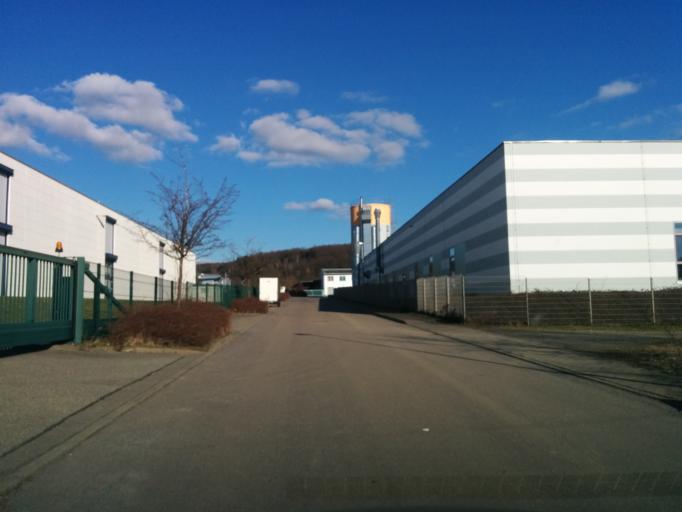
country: DE
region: Saxony
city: Falkenau
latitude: 50.8555
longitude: 13.1011
